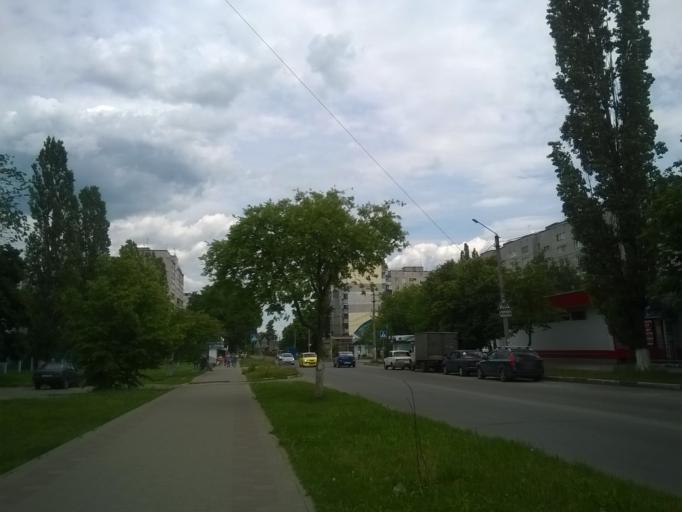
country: RU
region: Kursk
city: Kursk
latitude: 51.6739
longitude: 36.1556
